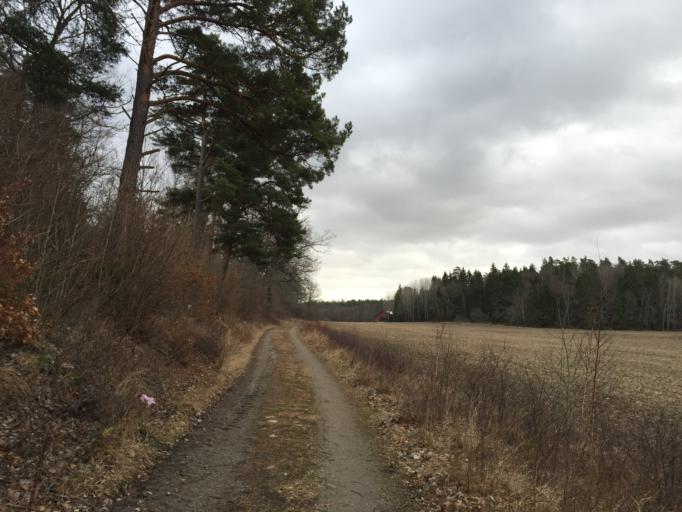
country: SE
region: Stockholm
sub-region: Salems Kommun
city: Ronninge
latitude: 59.2500
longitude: 17.7041
